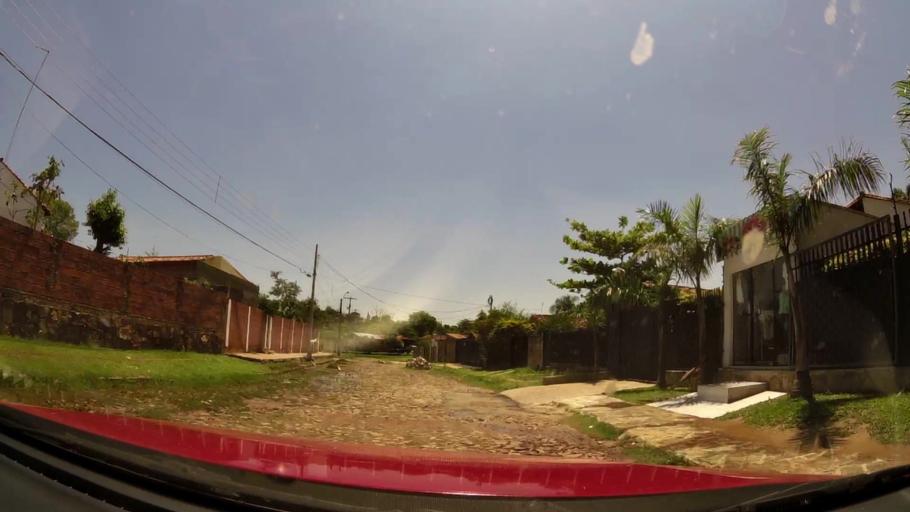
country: PY
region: Central
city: Colonia Mariano Roque Alonso
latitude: -25.2374
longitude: -57.5484
